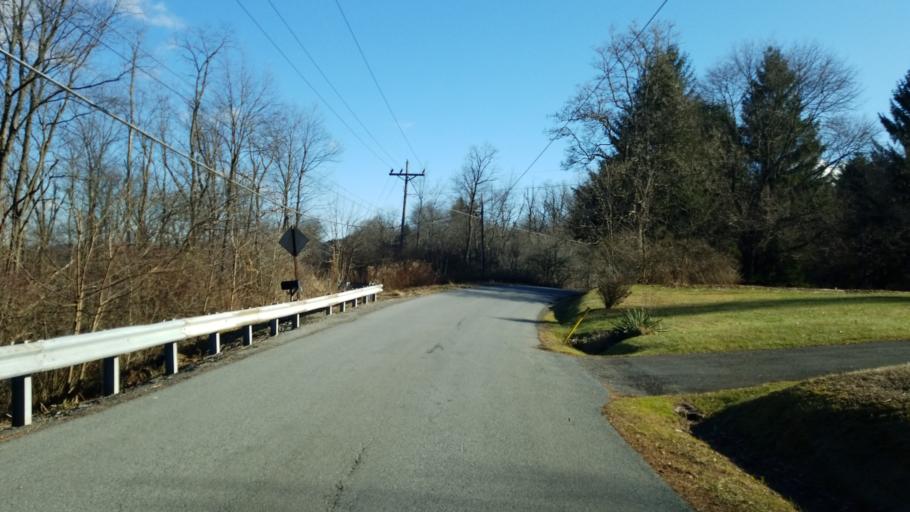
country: US
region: Pennsylvania
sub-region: Clearfield County
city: Hyde
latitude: 40.9833
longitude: -78.4850
